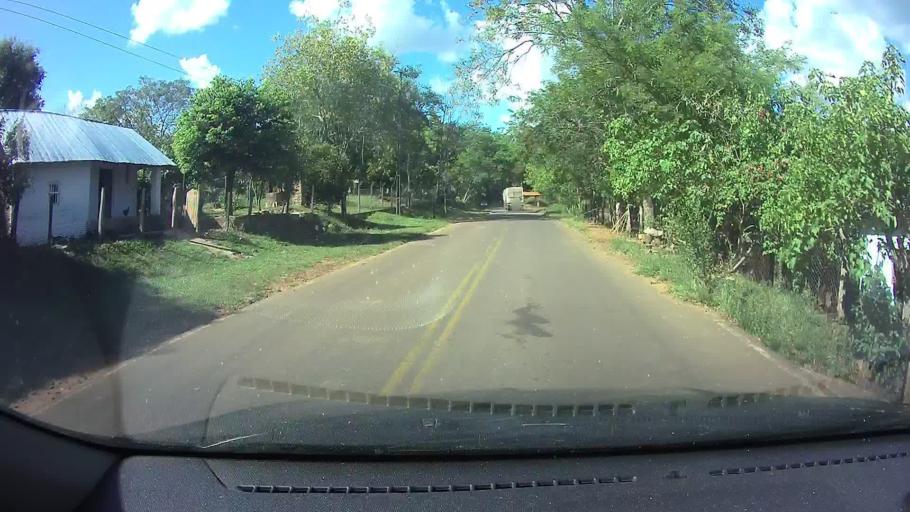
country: PY
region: Paraguari
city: Sapucai
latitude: -25.6705
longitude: -56.8616
